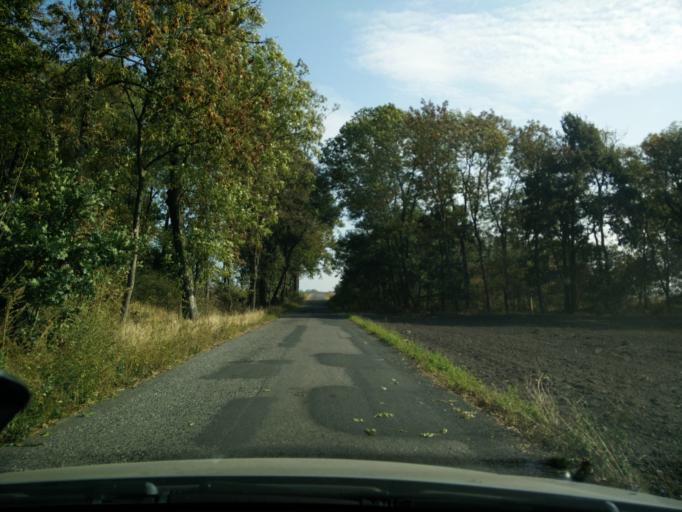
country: PL
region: Greater Poland Voivodeship
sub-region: Powiat sredzki
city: Sroda Wielkopolska
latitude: 52.3023
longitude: 17.2559
